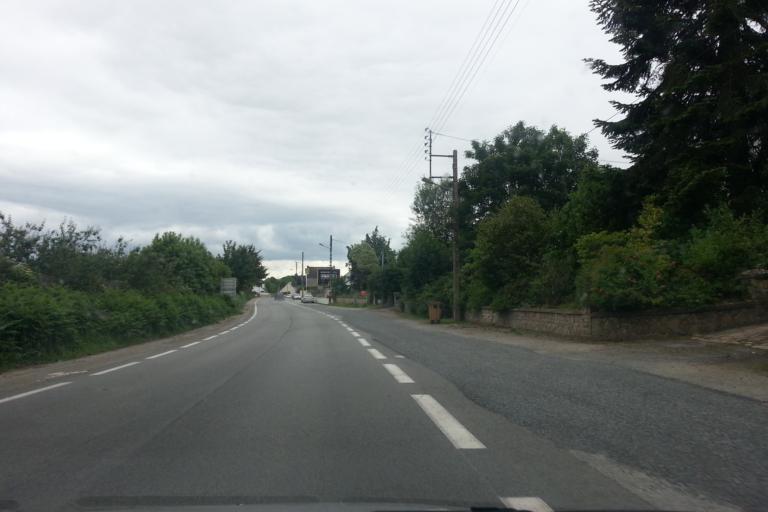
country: FR
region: Brittany
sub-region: Departement du Morbihan
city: Le Faouet
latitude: 48.0431
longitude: -3.4981
